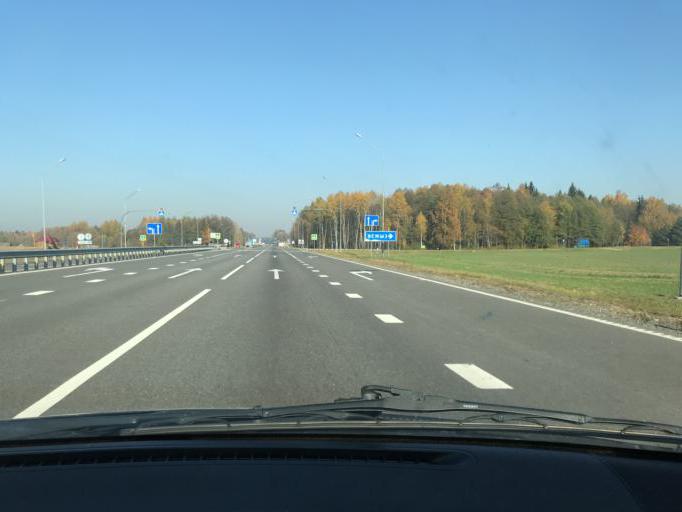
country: BY
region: Minsk
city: Slutsk
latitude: 53.2707
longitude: 27.5502
